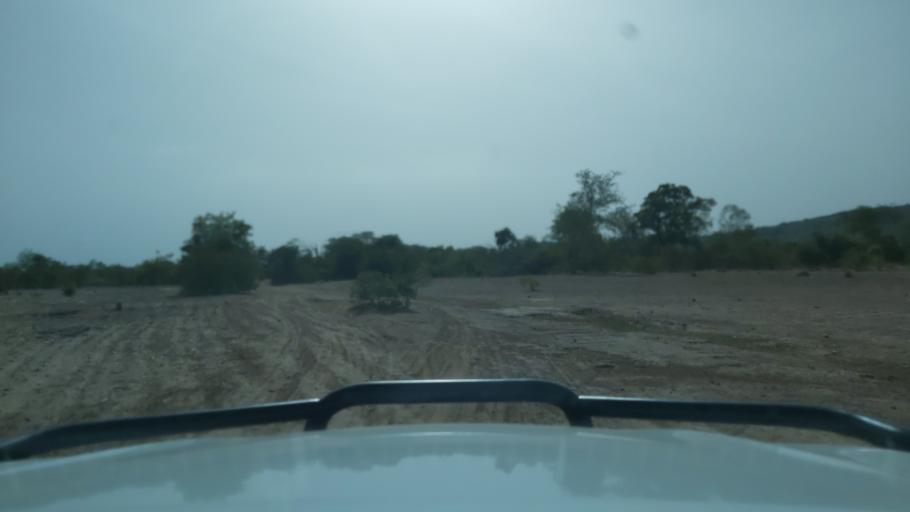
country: ML
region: Koulikoro
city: Koulikoro
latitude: 13.1760
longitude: -7.7495
